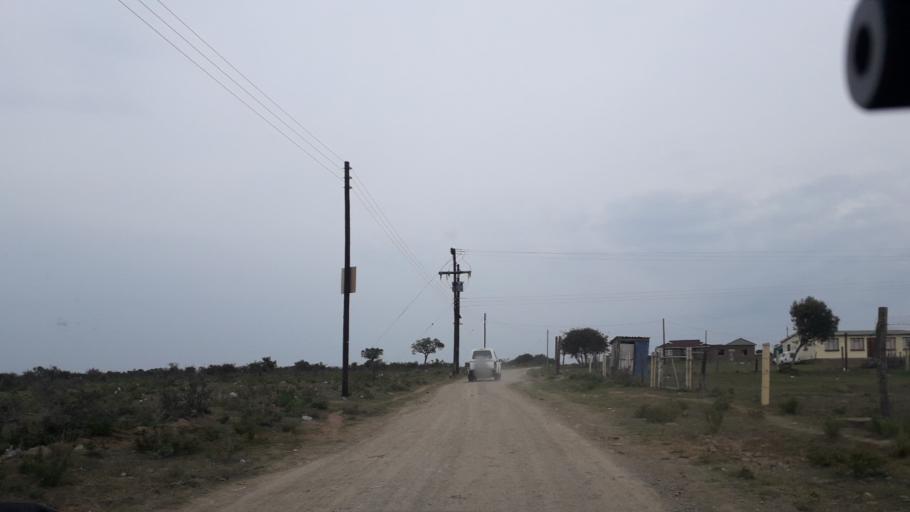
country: ZA
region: Eastern Cape
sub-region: Buffalo City Metropolitan Municipality
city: Bhisho
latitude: -32.8346
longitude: 27.3724
